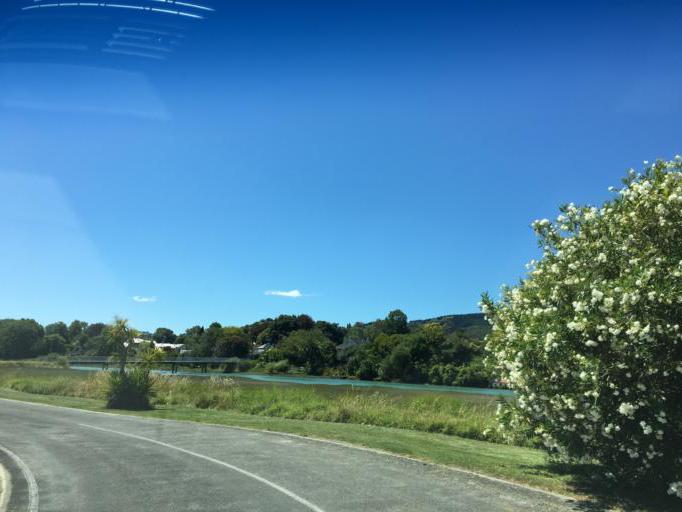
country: NZ
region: Gisborne
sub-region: Gisborne District
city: Gisborne
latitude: -38.6593
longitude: 178.0249
